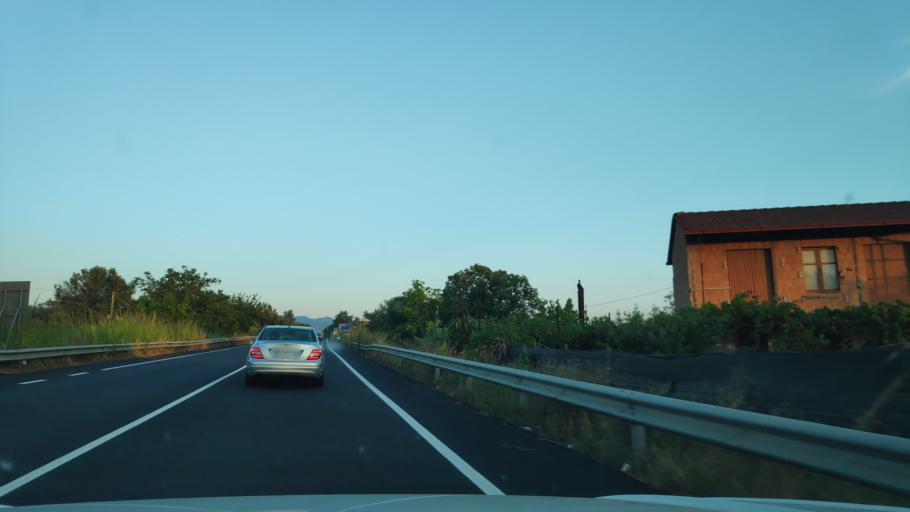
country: IT
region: Calabria
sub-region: Provincia di Reggio Calabria
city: Melicucco
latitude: 38.4370
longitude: 16.0468
